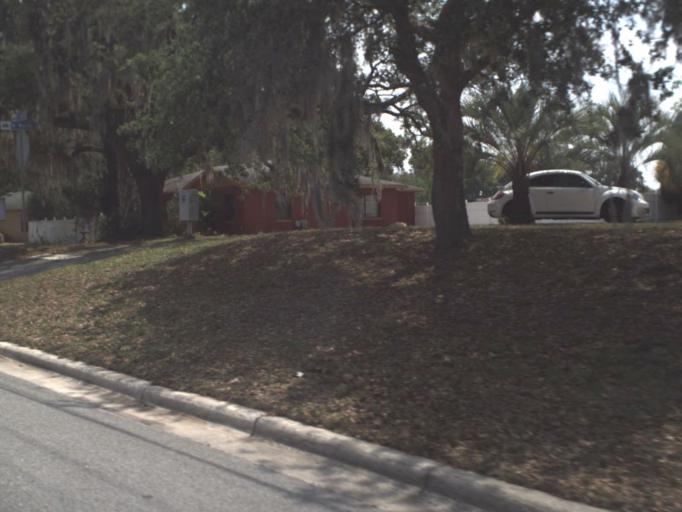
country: US
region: Florida
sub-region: Lake County
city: Howie In The Hills
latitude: 28.7121
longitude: -81.7722
